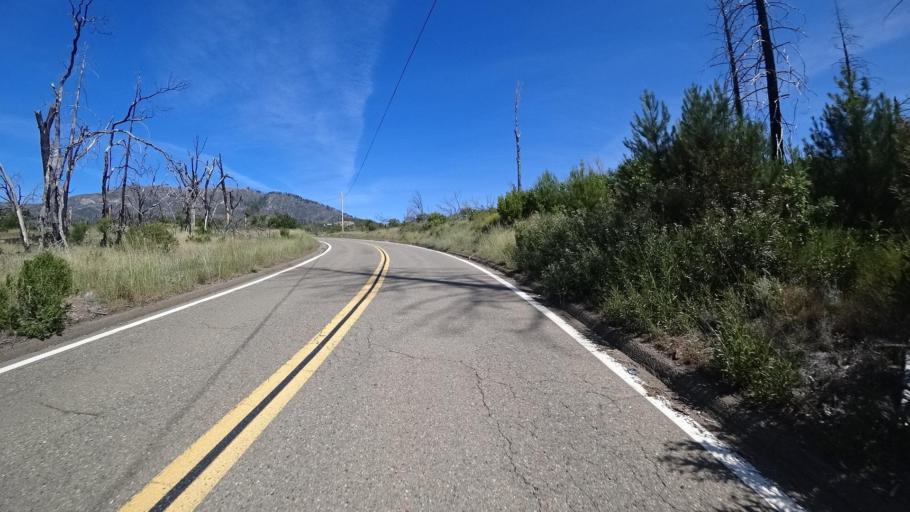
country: US
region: California
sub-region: Lake County
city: Cobb
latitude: 38.7816
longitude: -122.6914
